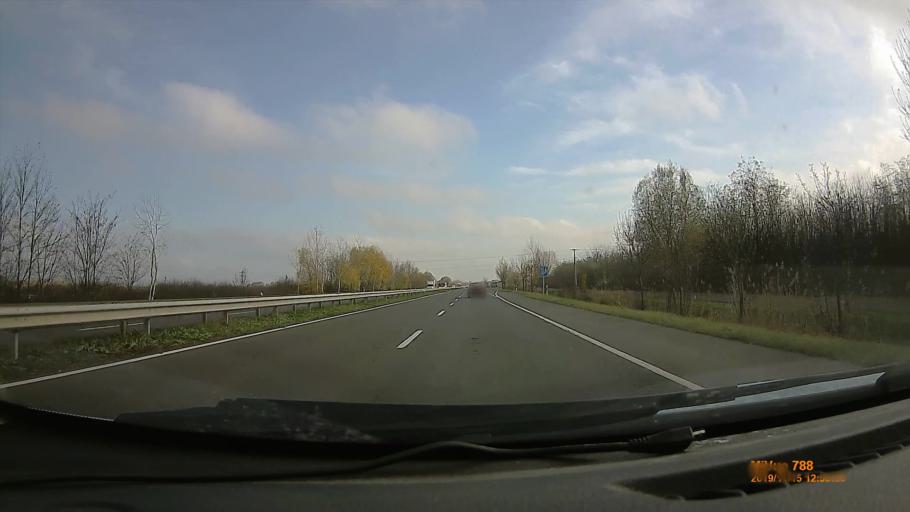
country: HU
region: Bekes
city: Doboz
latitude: 46.6684
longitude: 21.1889
